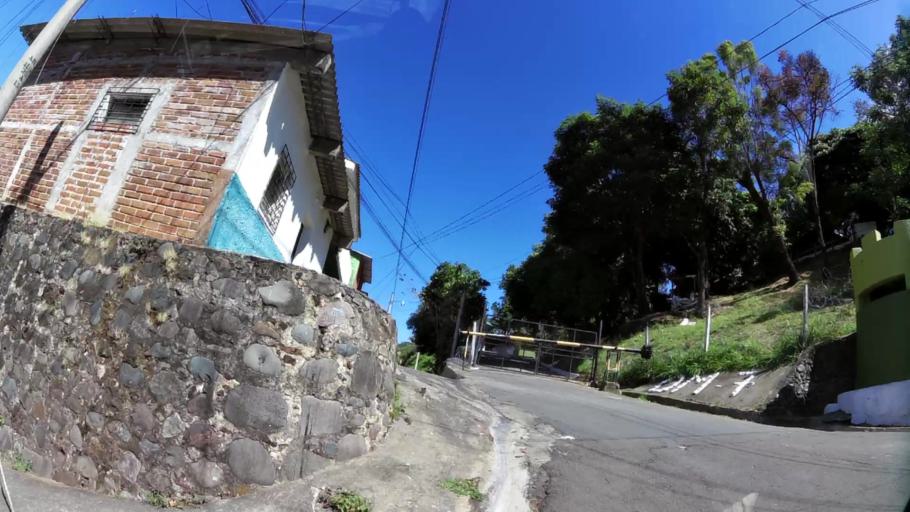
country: SV
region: Ahuachapan
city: Ahuachapan
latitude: 13.9201
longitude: -89.8446
